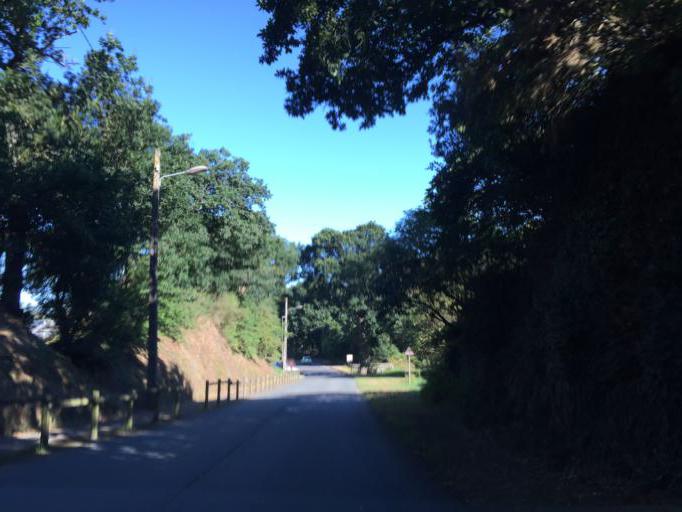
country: FR
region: Brittany
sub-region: Departement des Cotes-d'Armor
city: Jugon-les-Lacs
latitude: 48.4025
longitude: -2.3180
